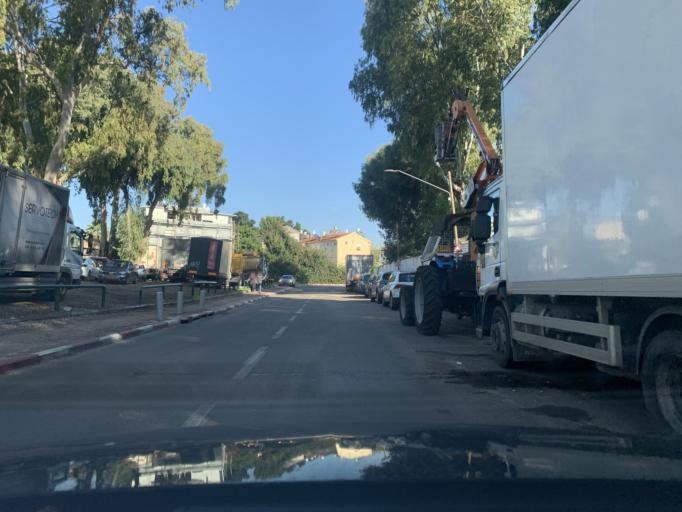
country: IL
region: Tel Aviv
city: Azor
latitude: 32.0464
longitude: 34.8155
